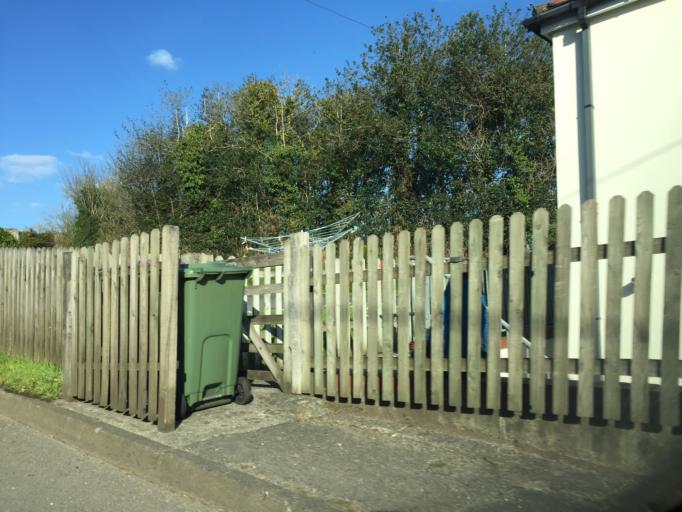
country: GB
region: Wales
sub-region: Torfaen County Borough
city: New Inn
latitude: 51.6867
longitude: -3.0049
